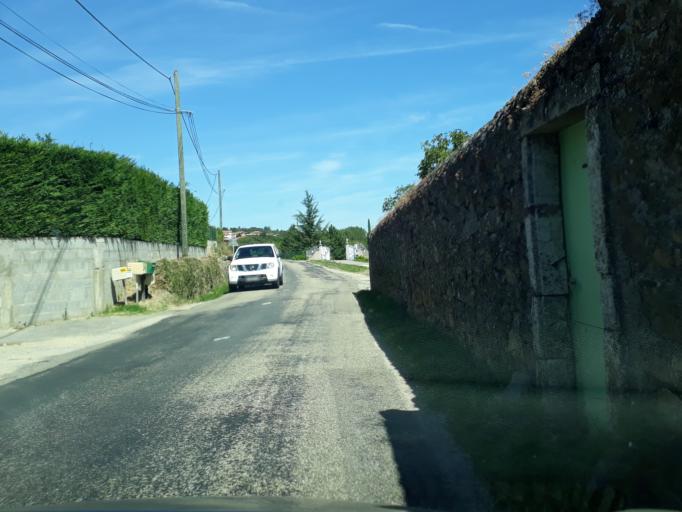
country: FR
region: Rhone-Alpes
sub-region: Departement de l'Ardeche
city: Felines
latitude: 45.3084
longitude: 4.7295
